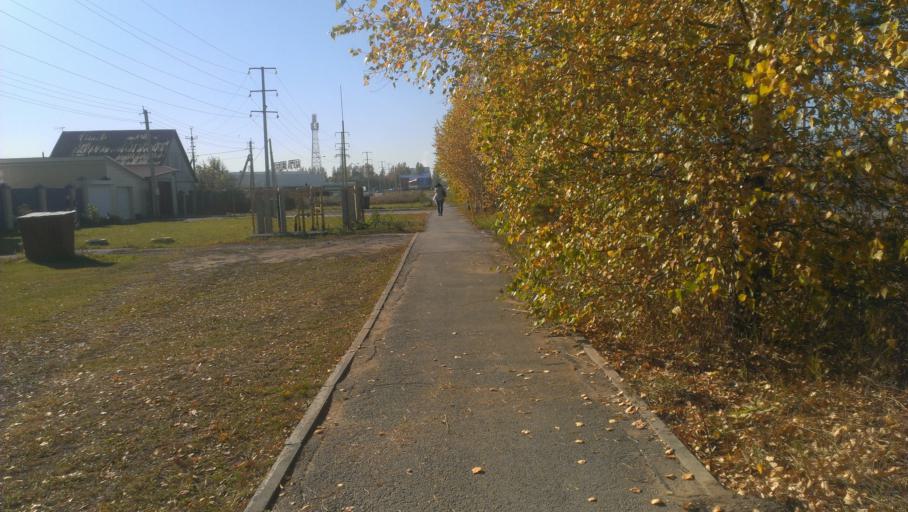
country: RU
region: Altai Krai
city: Novosilikatnyy
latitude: 53.3529
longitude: 83.6330
